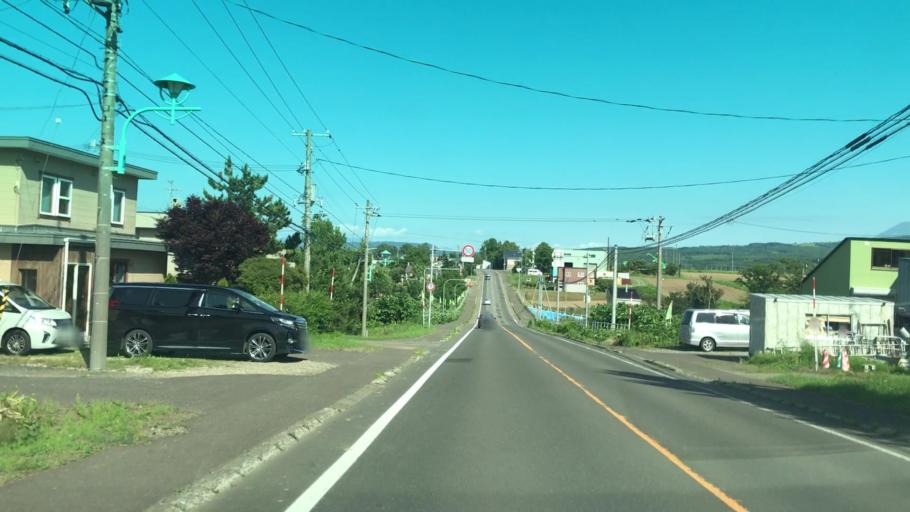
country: JP
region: Hokkaido
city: Iwanai
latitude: 42.9807
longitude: 140.5768
